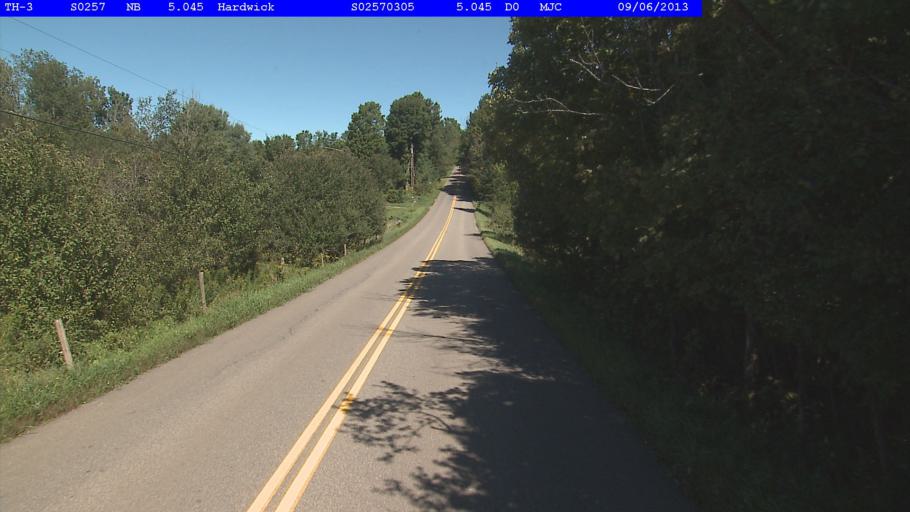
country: US
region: Vermont
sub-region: Caledonia County
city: Hardwick
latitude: 44.5590
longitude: -72.3136
